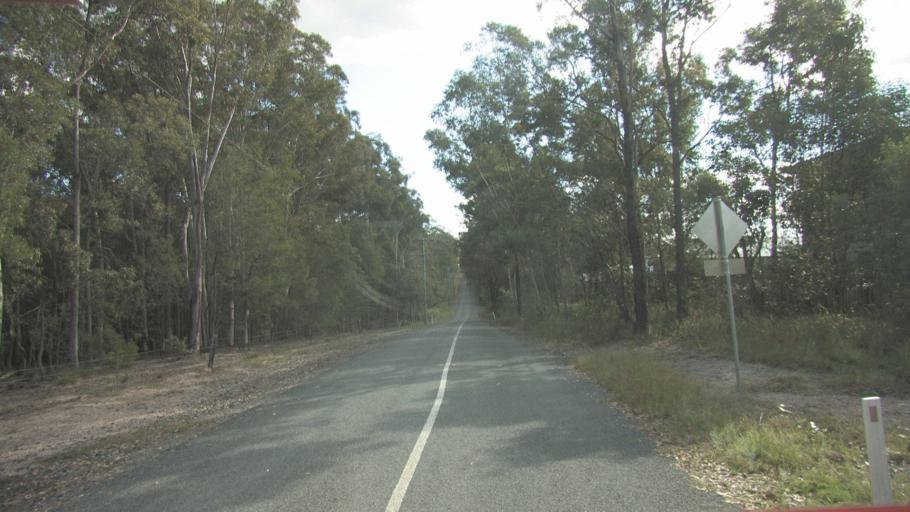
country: AU
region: Queensland
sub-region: Redland
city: Redland Bay
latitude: -27.6539
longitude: 153.2612
